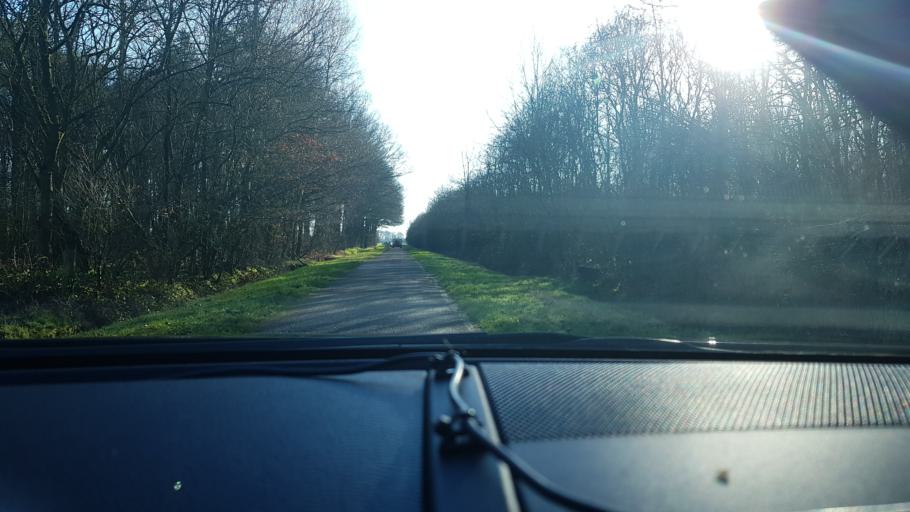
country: NL
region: Limburg
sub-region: Gemeente Leudal
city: Haelen
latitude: 51.2813
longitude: 5.9841
